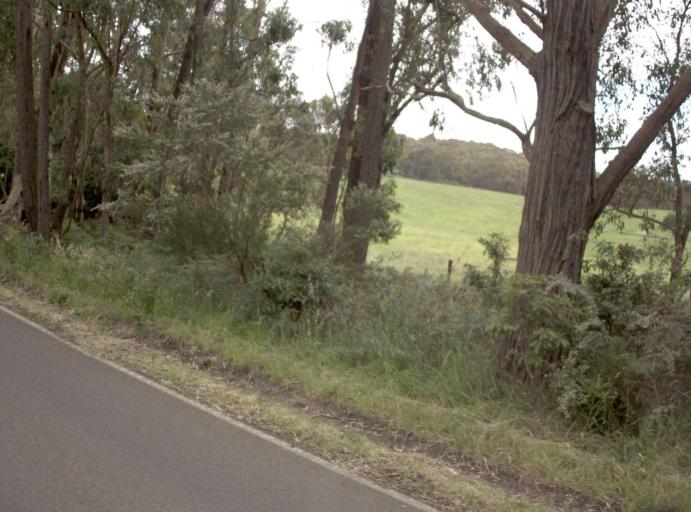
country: AU
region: Victoria
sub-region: Latrobe
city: Moe
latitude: -38.0258
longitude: 146.1612
